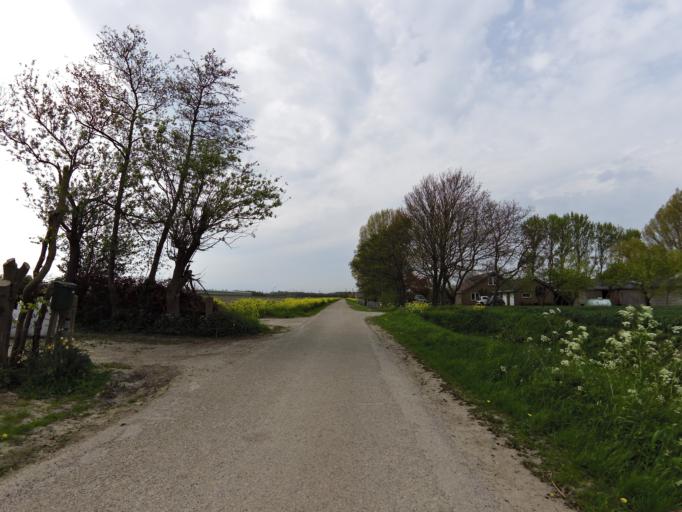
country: NL
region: South Holland
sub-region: Gemeente Brielle
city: Brielle
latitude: 51.9154
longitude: 4.1606
